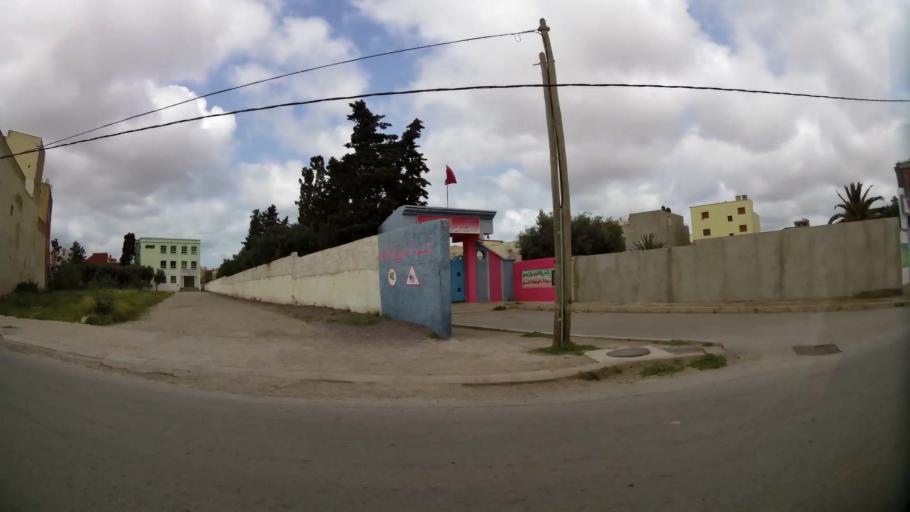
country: MA
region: Oriental
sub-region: Nador
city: Nador
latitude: 35.1643
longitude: -2.9413
